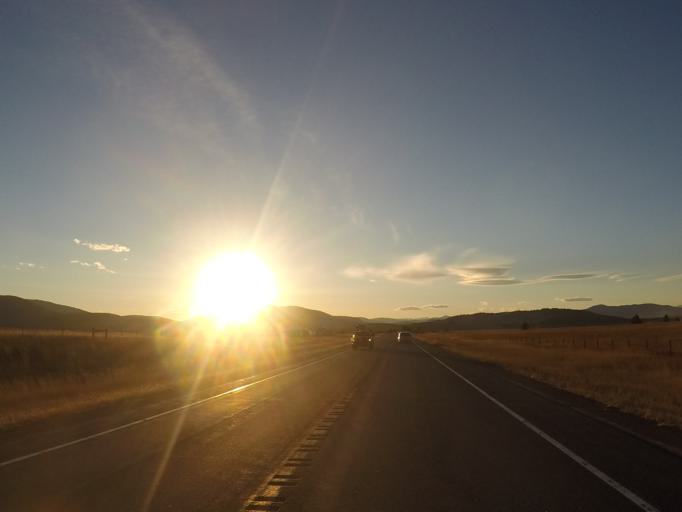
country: US
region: Montana
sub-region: Missoula County
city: Seeley Lake
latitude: 47.0201
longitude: -113.1141
